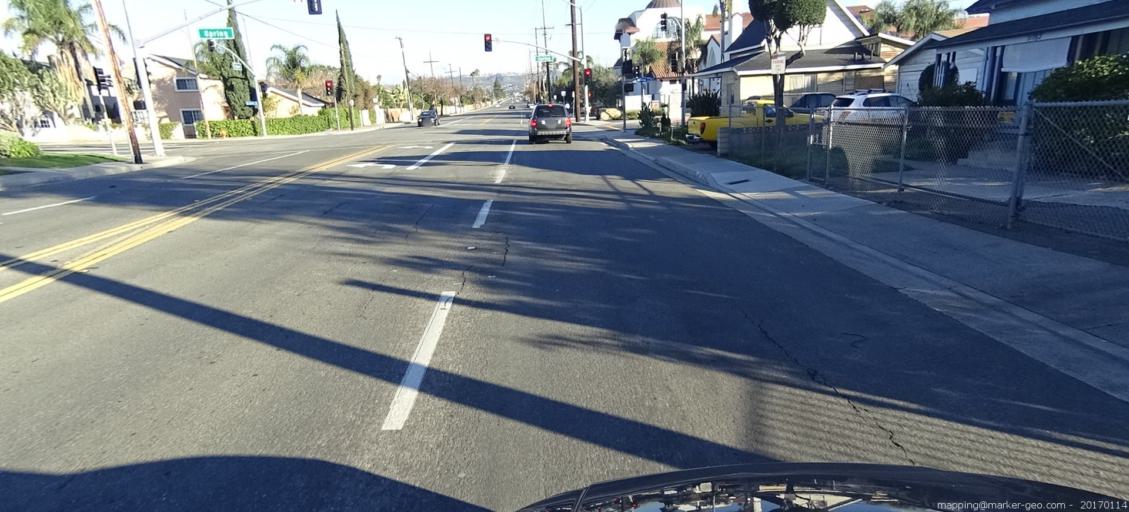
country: US
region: California
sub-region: Orange County
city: Villa Park
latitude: 33.7909
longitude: -117.8056
